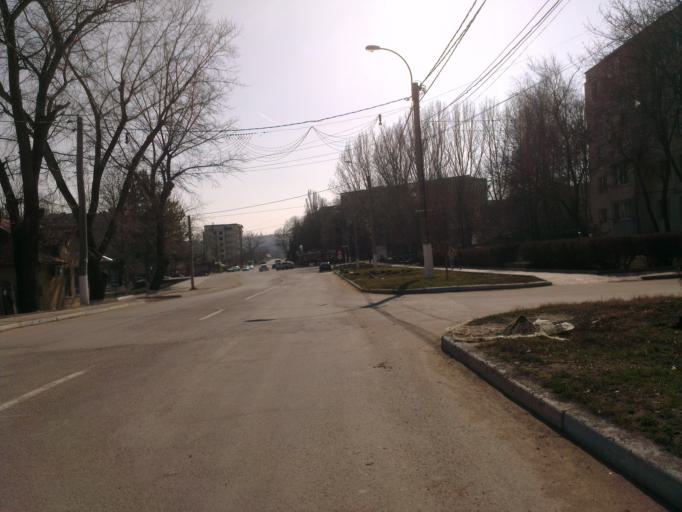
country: MD
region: Chisinau
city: Cricova
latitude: 47.1407
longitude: 28.8648
